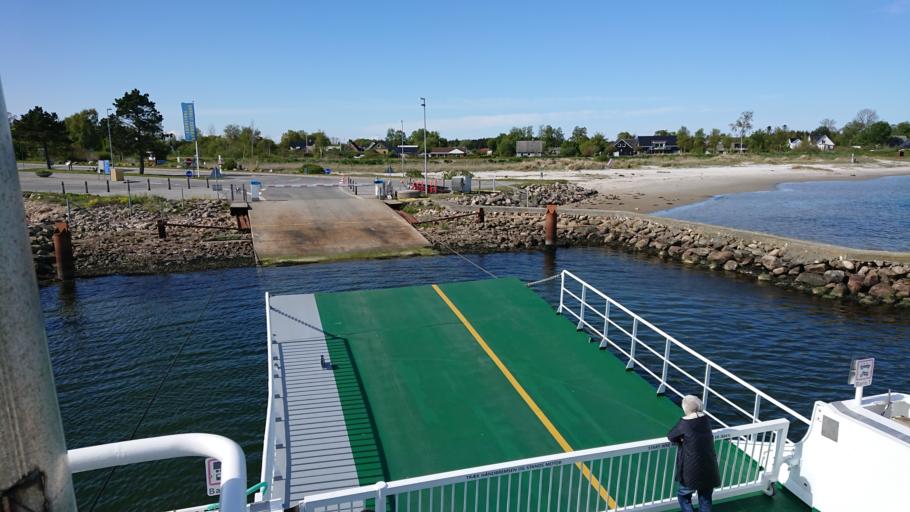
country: DK
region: Central Jutland
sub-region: Norddjurs Kommune
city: Allingabro
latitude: 56.6091
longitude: 10.3005
